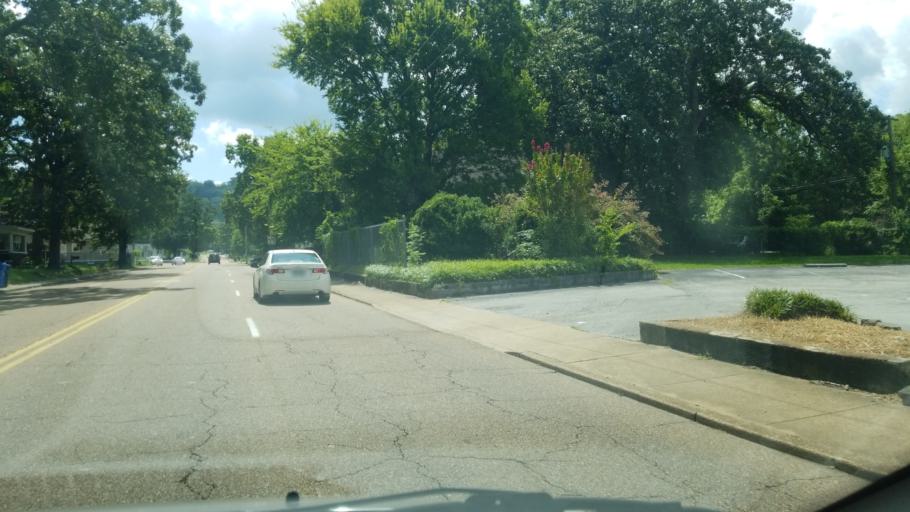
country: US
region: Tennessee
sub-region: Hamilton County
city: East Ridge
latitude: 35.0310
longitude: -85.2698
